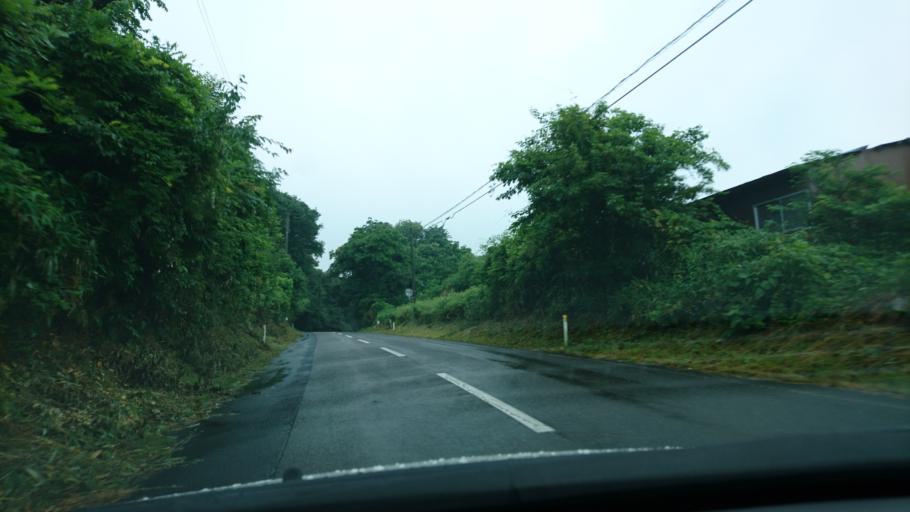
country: JP
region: Iwate
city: Ichinoseki
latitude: 38.9089
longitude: 141.0318
